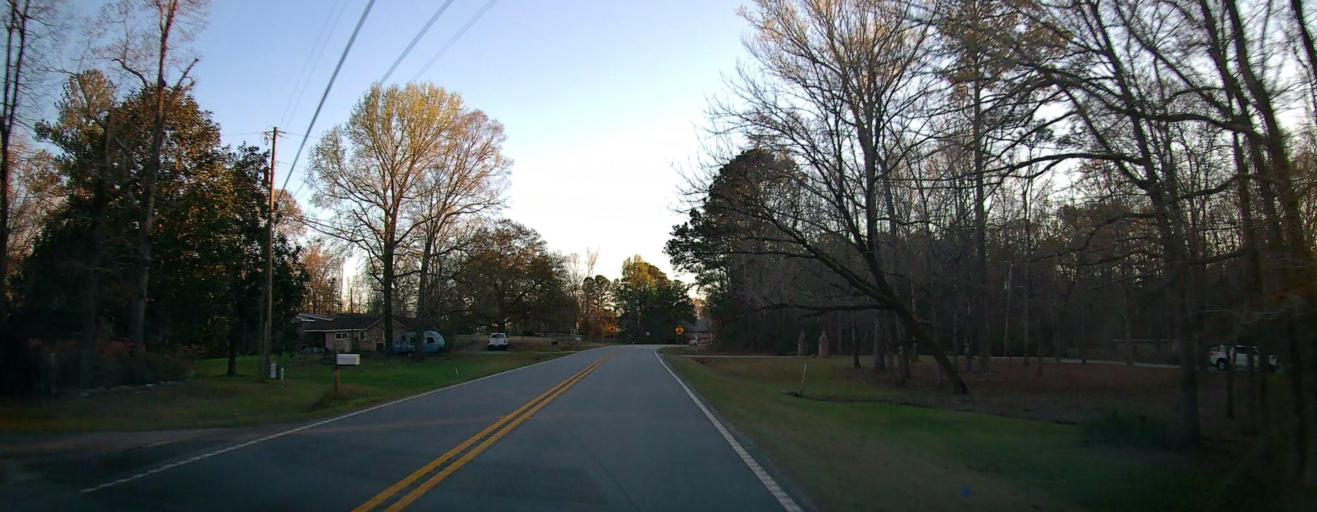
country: US
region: Alabama
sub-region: Lee County
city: Smiths Station
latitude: 32.6285
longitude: -85.0346
